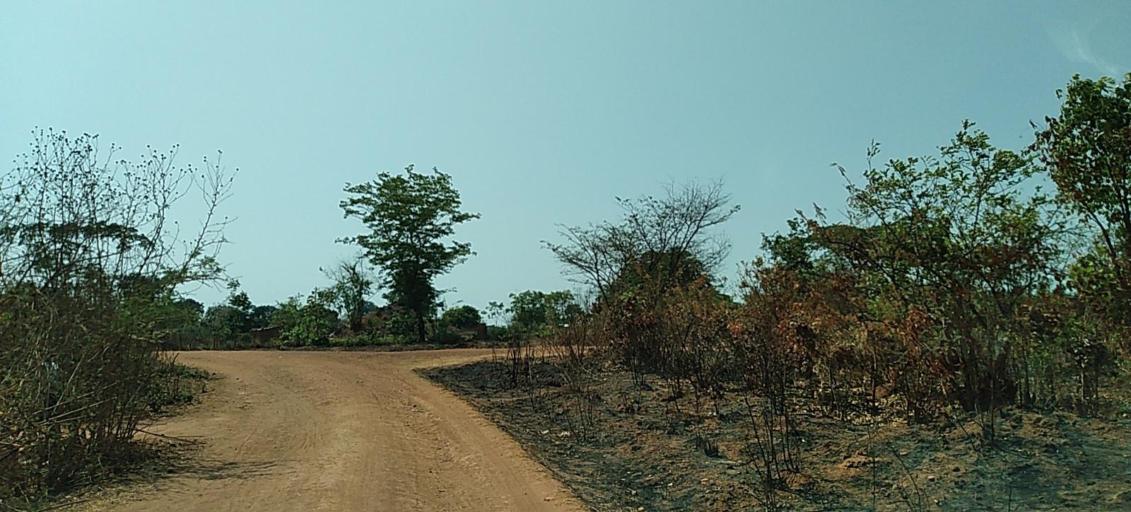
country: ZM
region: Copperbelt
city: Luanshya
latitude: -13.3492
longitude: 28.4006
